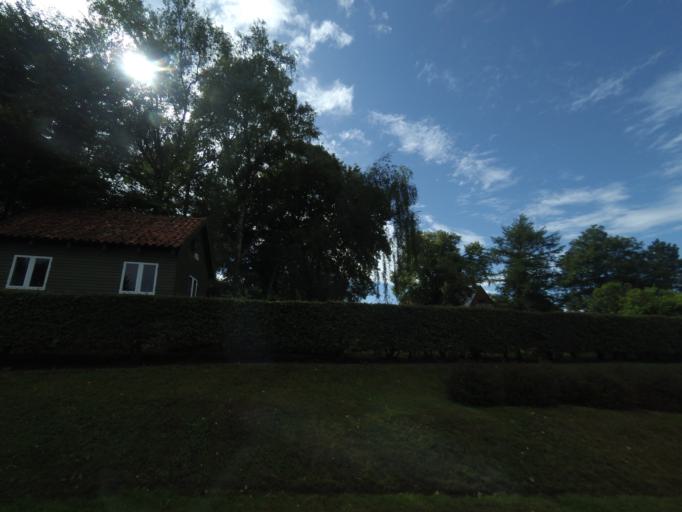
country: DK
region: South Denmark
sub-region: Assens Kommune
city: Vissenbjerg
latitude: 55.4446
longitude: 10.1838
